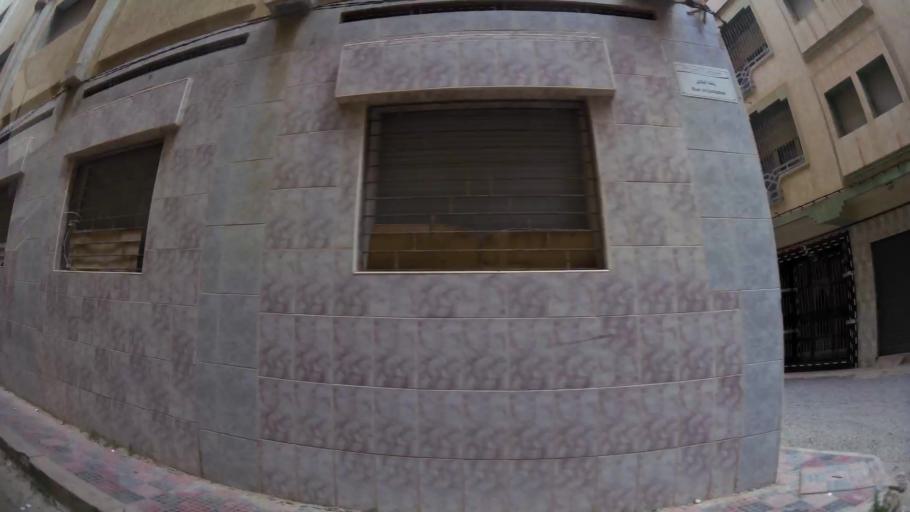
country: MA
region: Oriental
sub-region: Nador
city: Nador
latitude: 35.1622
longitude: -2.9253
